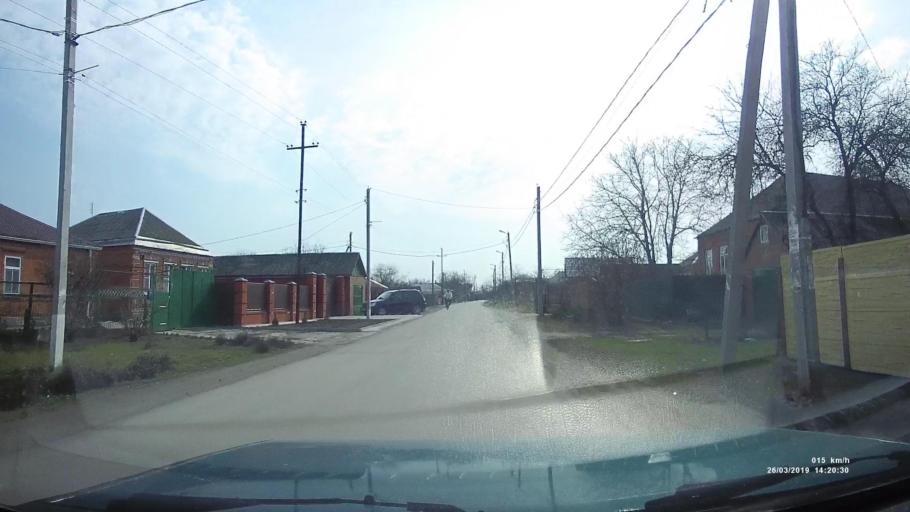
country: RU
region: Rostov
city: Novobessergenovka
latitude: 47.1897
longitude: 38.8705
